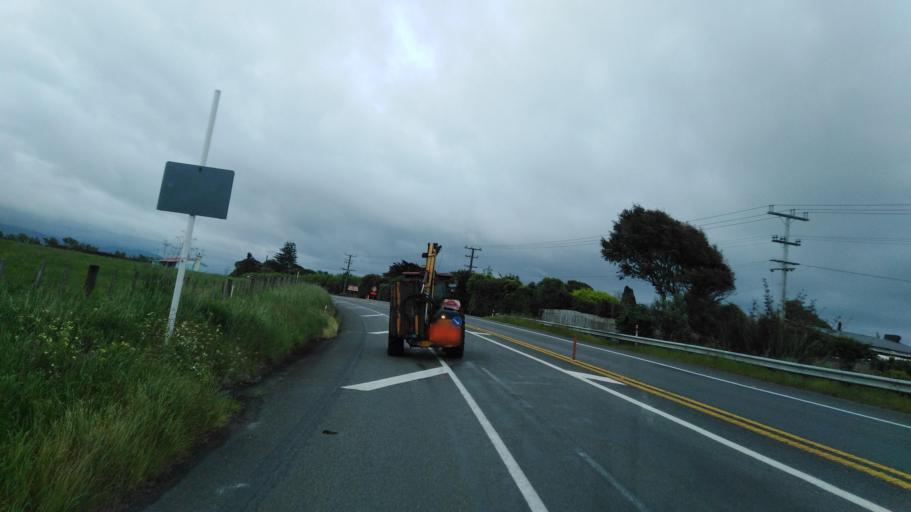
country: NZ
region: Wellington
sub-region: Kapiti Coast District
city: Otaki
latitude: -40.7431
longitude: 175.1705
